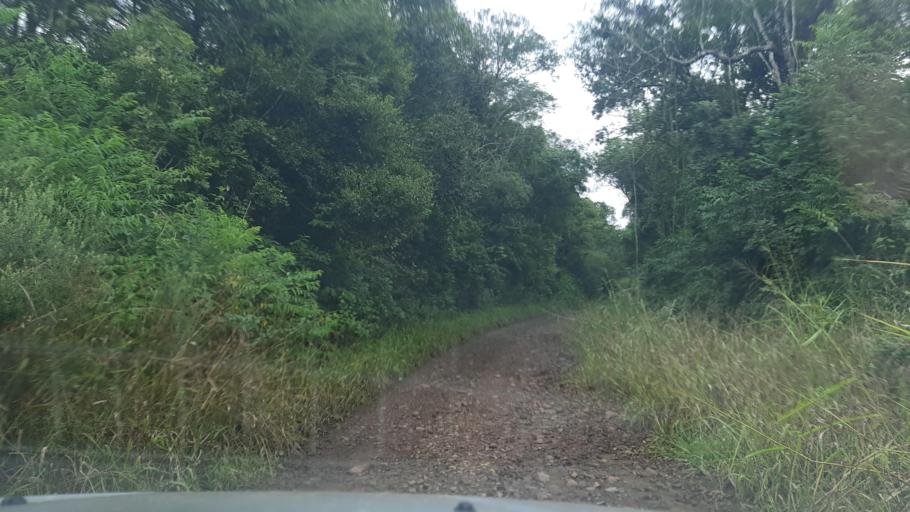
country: BR
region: Parana
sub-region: Ampere
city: Ampere
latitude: -26.0492
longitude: -53.5214
